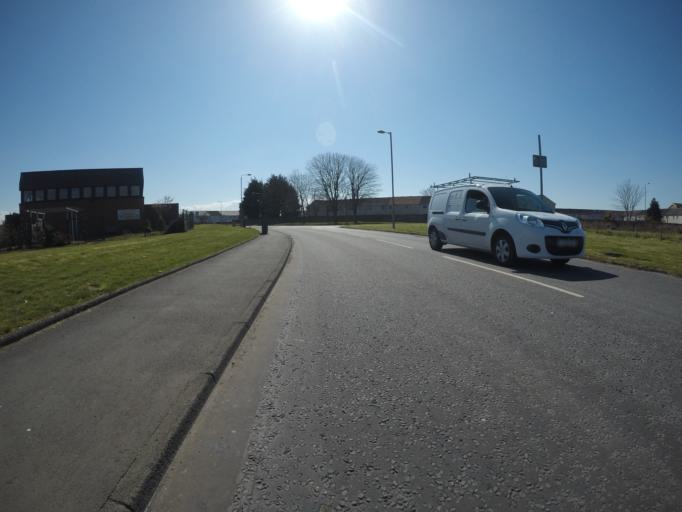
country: GB
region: Scotland
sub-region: North Ayrshire
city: Irvine
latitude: 55.6301
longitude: -4.6676
